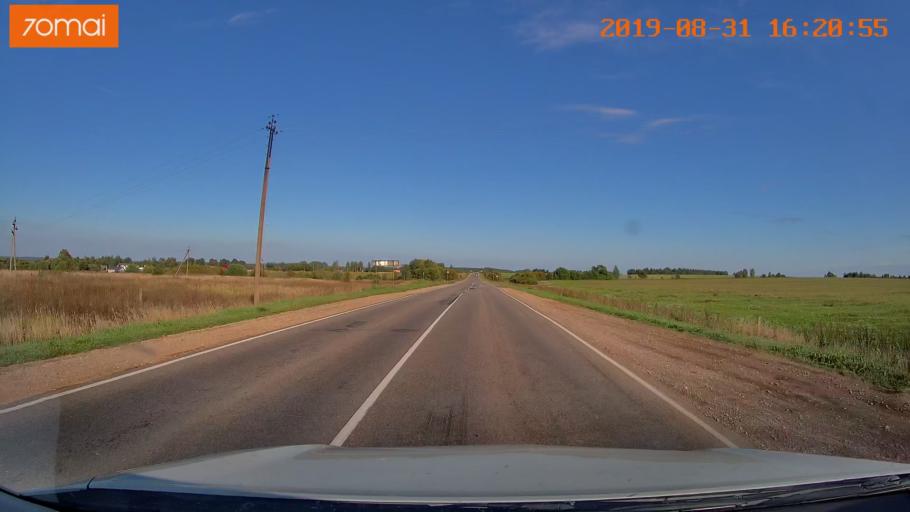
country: RU
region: Kaluga
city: Babynino
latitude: 54.5226
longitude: 35.6172
